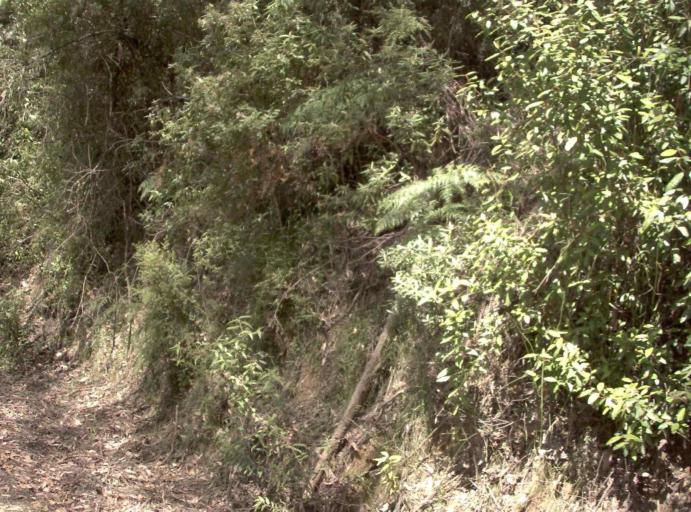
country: AU
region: Victoria
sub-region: Latrobe
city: Morwell
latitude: -38.4352
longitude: 146.5275
